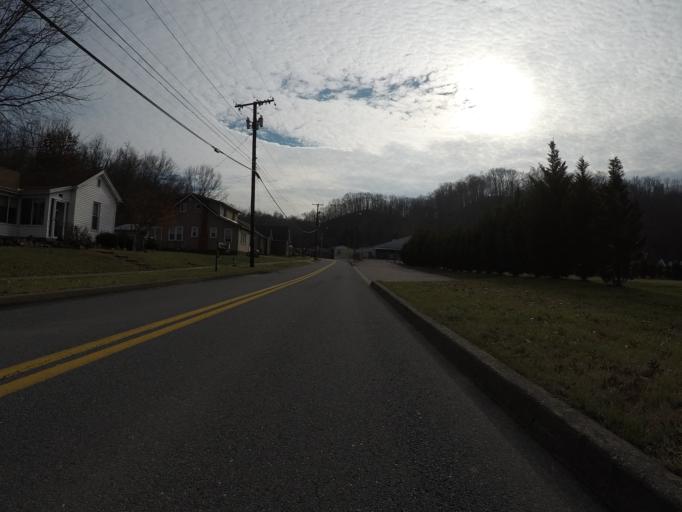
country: US
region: West Virginia
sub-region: Cabell County
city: Barboursville
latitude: 38.4023
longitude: -82.2936
